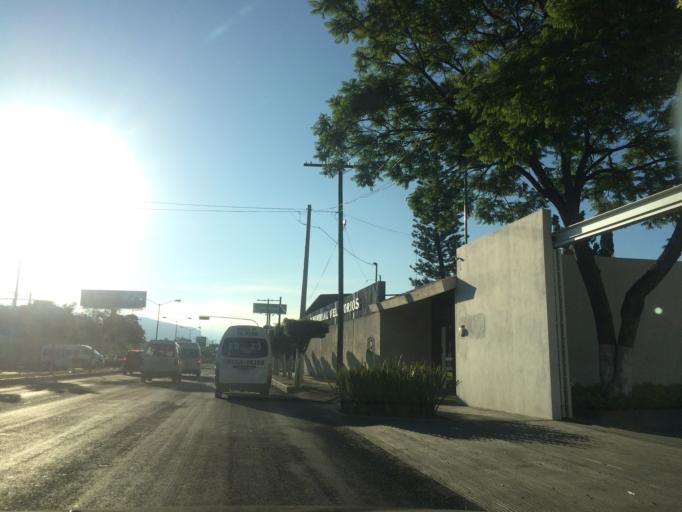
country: MX
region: Puebla
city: Tehuacan
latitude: 18.4633
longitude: -97.4048
